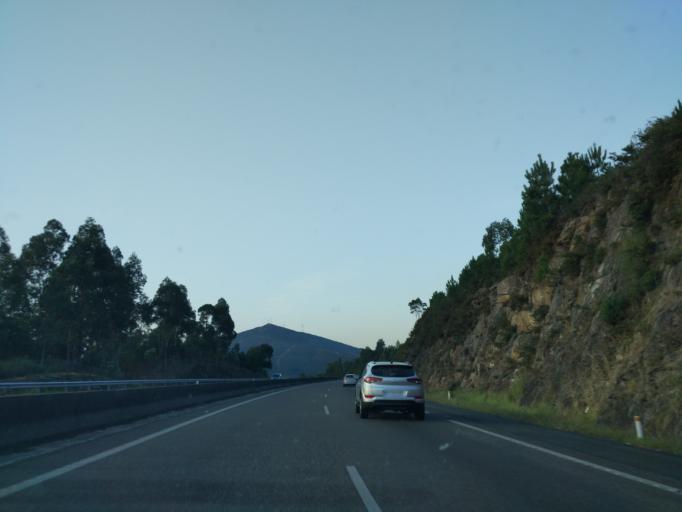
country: ES
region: Galicia
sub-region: Provincia de Pontevedra
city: Valga
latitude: 42.7171
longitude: -8.6430
